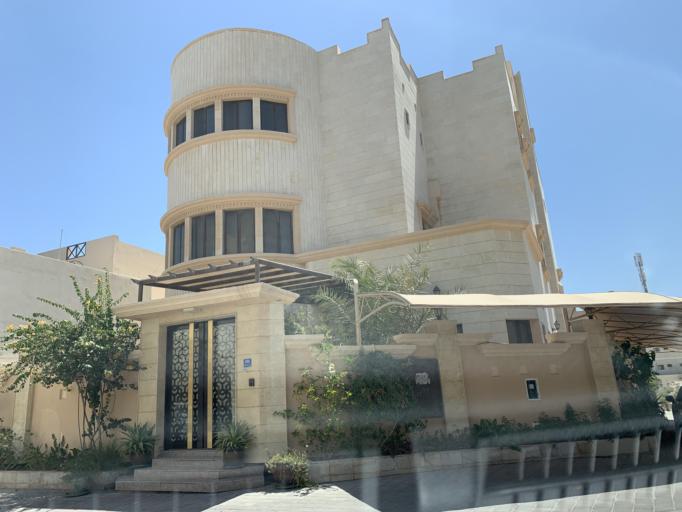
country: BH
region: Manama
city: Jidd Hafs
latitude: 26.2322
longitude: 50.4863
